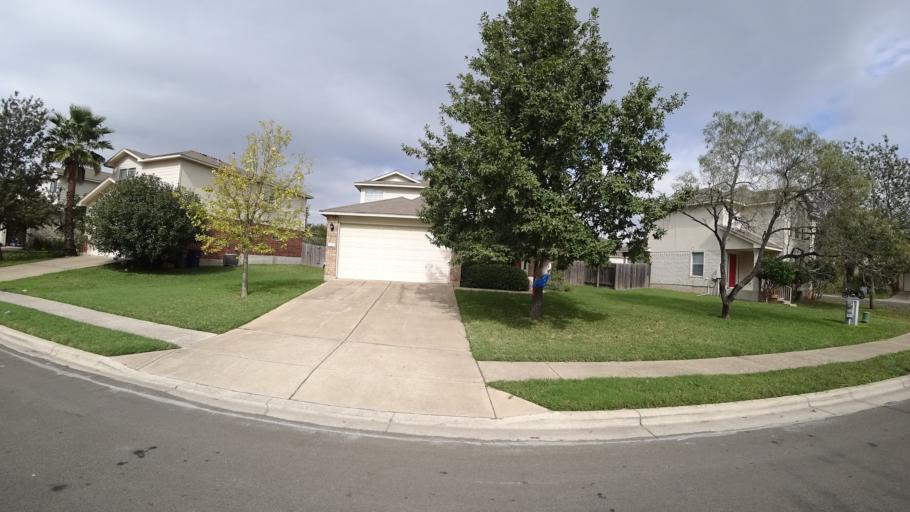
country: US
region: Texas
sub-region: Travis County
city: Manchaca
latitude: 30.1520
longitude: -97.8446
